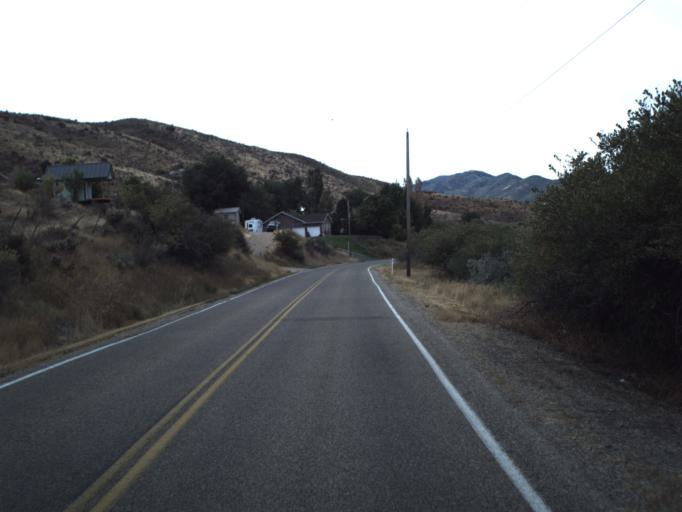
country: US
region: Utah
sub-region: Morgan County
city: Morgan
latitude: 41.0058
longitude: -111.6758
